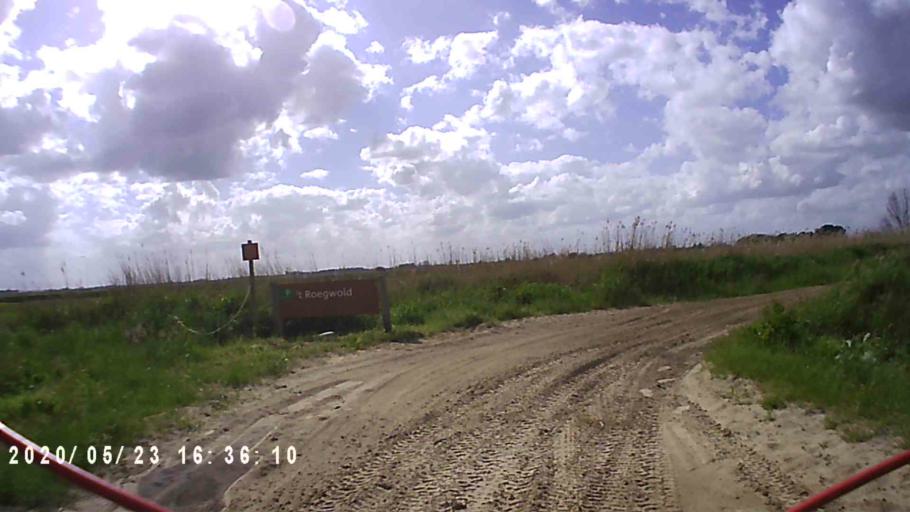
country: NL
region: Groningen
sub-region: Gemeente Slochteren
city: Slochteren
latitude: 53.2630
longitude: 6.8310
